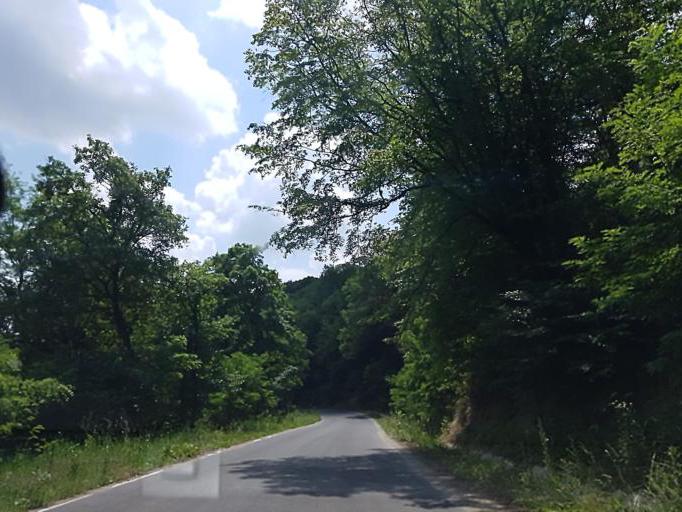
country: RO
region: Sibiu
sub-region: Comuna Seica Mare
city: Seica Mare
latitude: 46.0402
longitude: 24.1587
